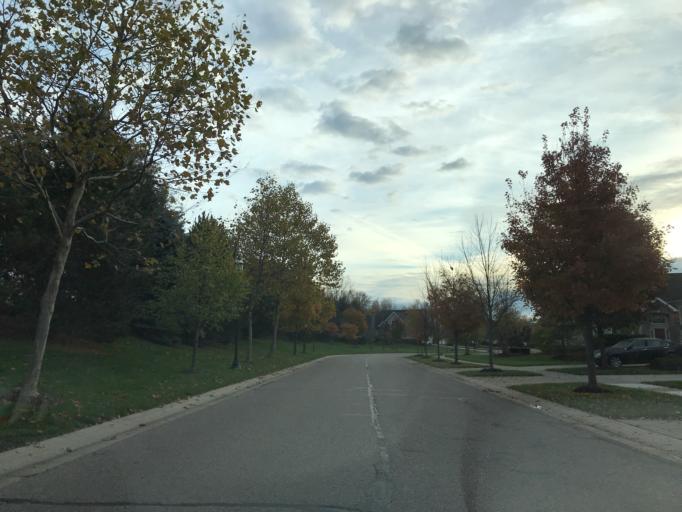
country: US
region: Michigan
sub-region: Oakland County
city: Wixom
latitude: 42.4803
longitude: -83.5504
